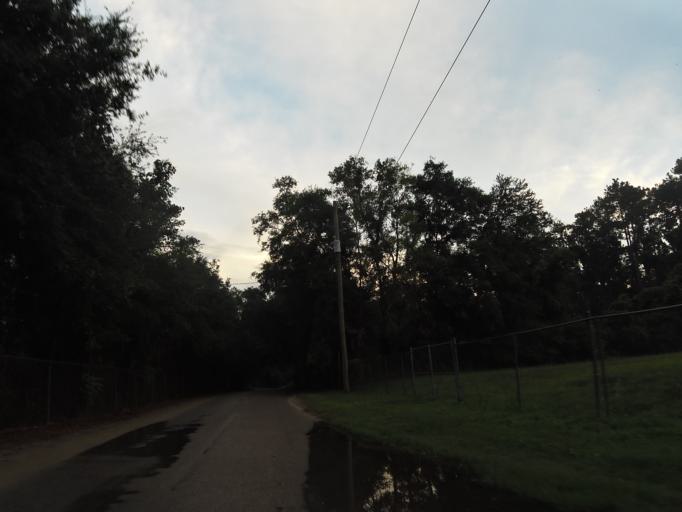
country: US
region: Florida
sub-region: Duval County
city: Jacksonville
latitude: 30.2710
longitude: -81.6396
